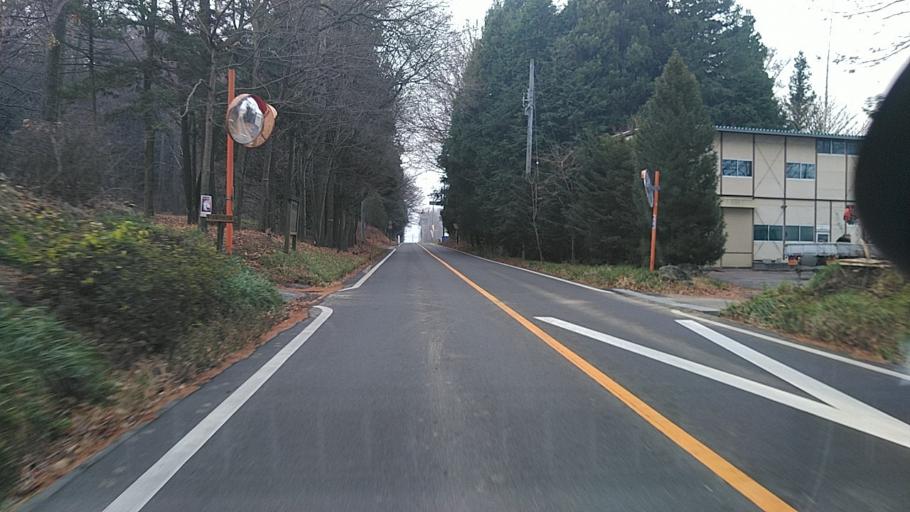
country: JP
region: Nagano
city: Shiojiri
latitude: 36.1461
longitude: 137.9917
